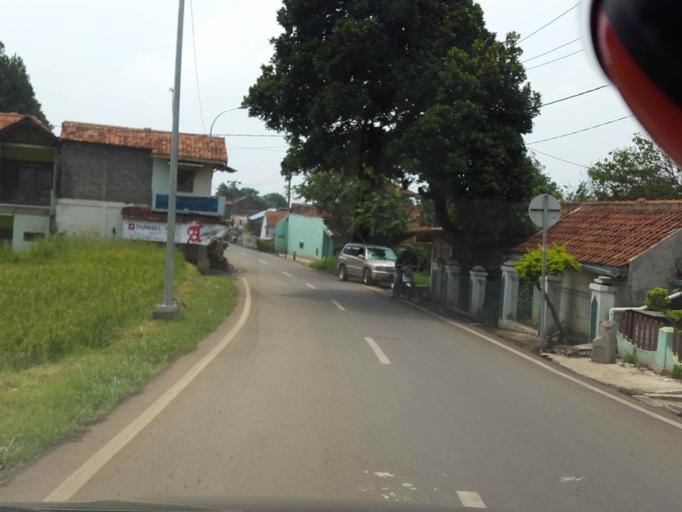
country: ID
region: West Java
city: Padalarang
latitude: -6.8411
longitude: 107.5025
